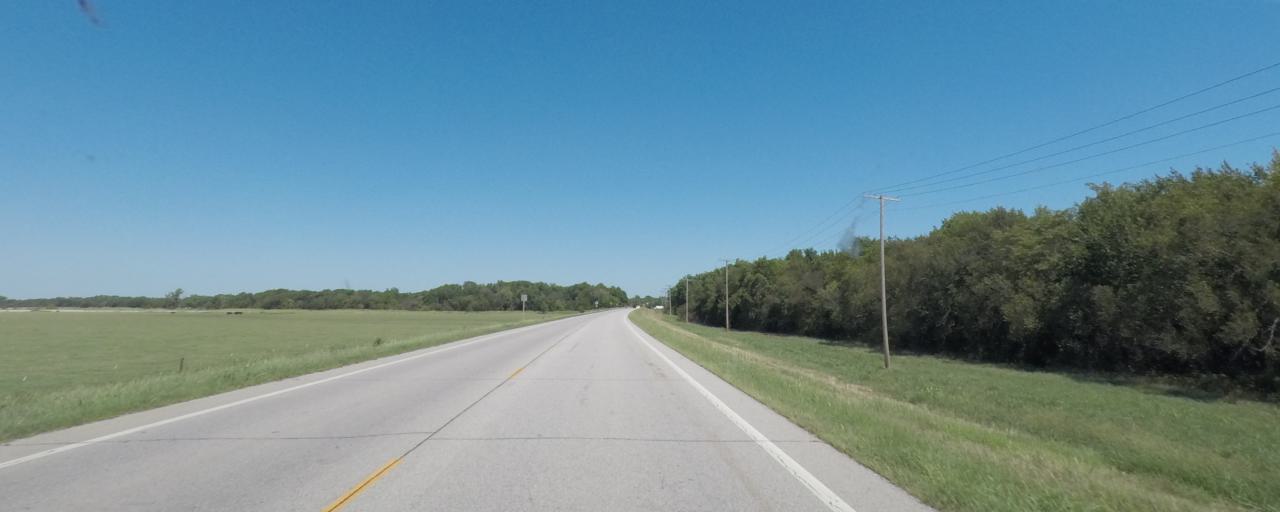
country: US
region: Kansas
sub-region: Sumner County
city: Wellington
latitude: 37.2460
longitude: -97.4032
